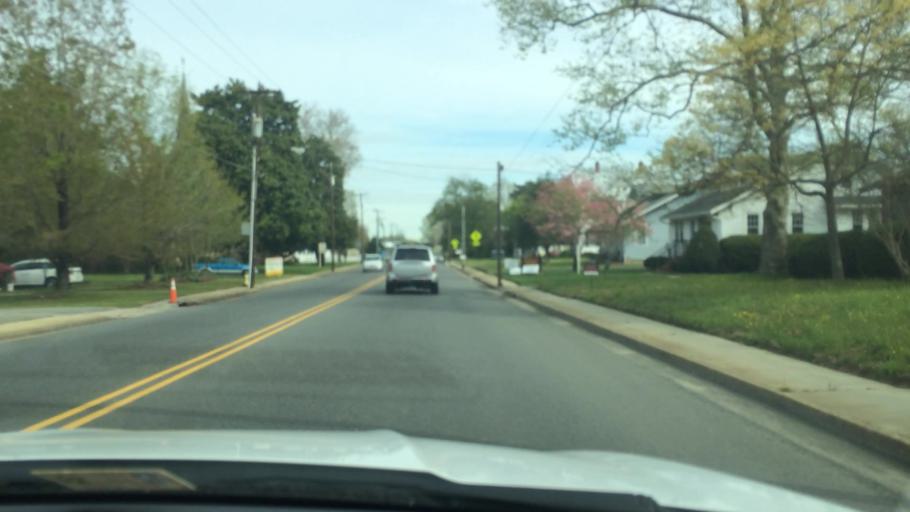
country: US
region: Virginia
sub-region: Lancaster County
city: Kilmarnock
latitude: 37.7057
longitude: -76.3786
